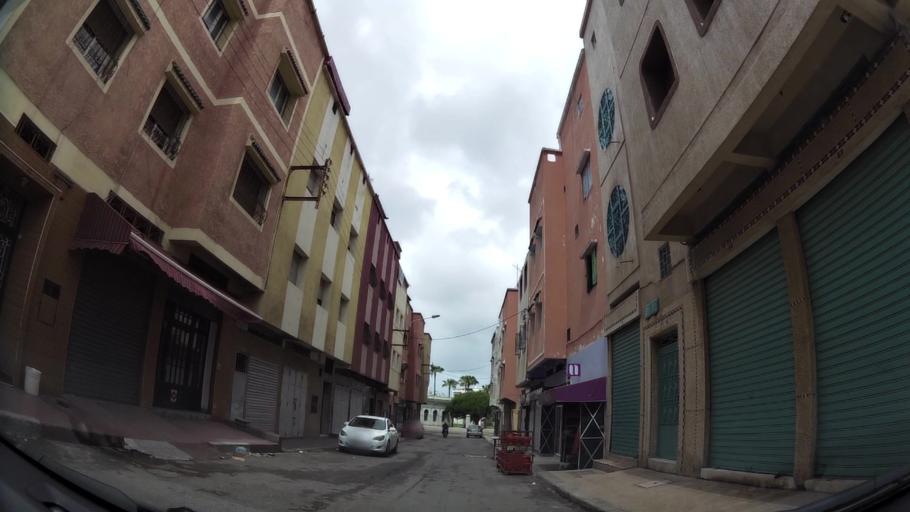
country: MA
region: Grand Casablanca
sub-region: Casablanca
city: Casablanca
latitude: 33.5423
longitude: -7.5821
